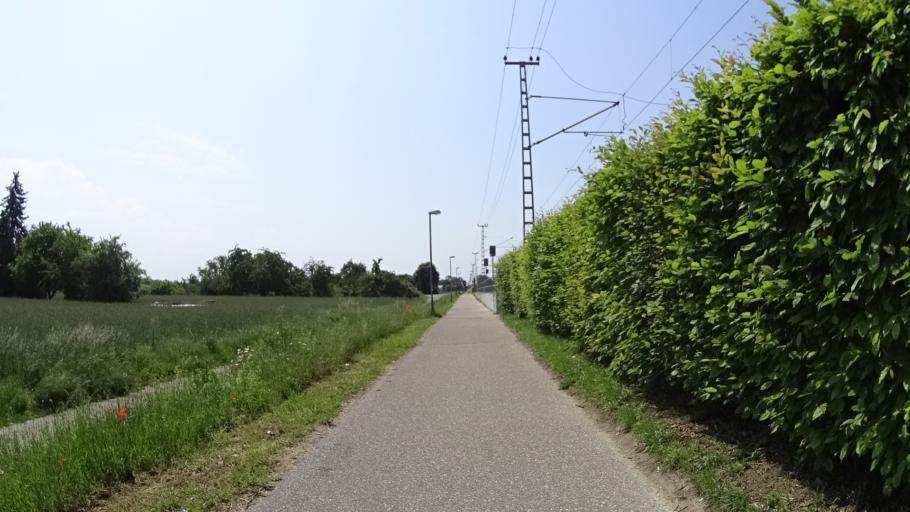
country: DE
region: Baden-Wuerttemberg
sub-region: Karlsruhe Region
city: Eggenstein-Leopoldshafen
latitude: 49.0805
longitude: 8.4001
